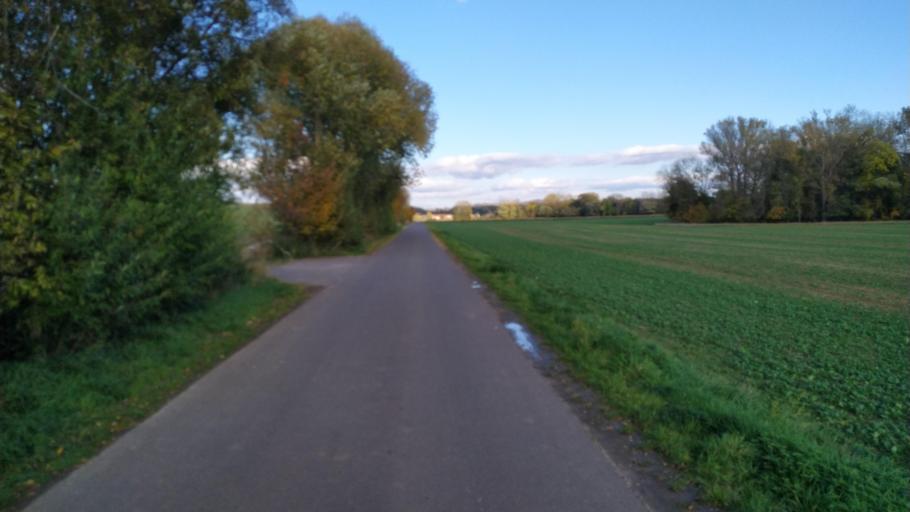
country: DE
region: Thuringia
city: Rannstedt
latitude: 51.0663
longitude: 11.5573
